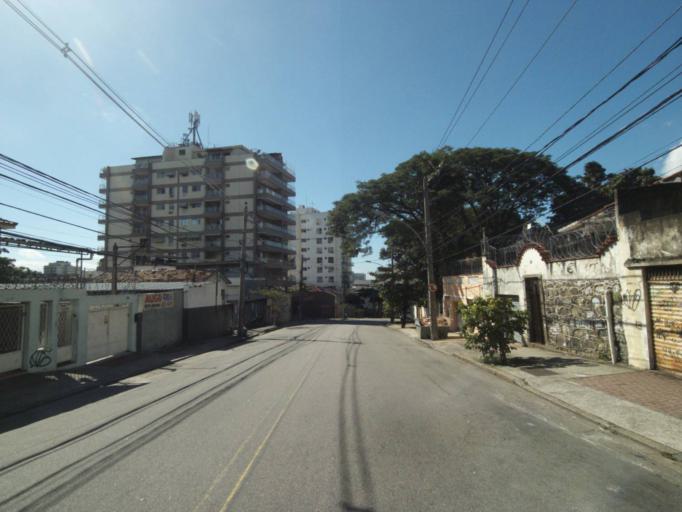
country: BR
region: Rio de Janeiro
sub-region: Rio De Janeiro
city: Rio de Janeiro
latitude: -22.9089
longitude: -43.2802
